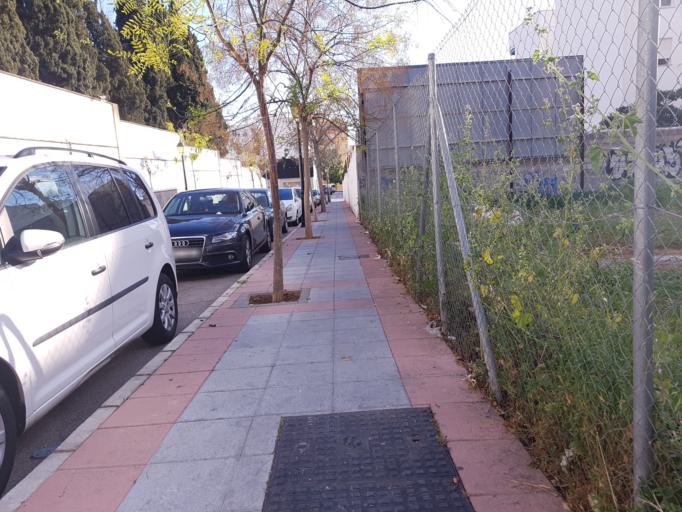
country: ES
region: Andalusia
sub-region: Provincia de Malaga
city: Marbella
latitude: 36.5159
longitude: -4.8781
